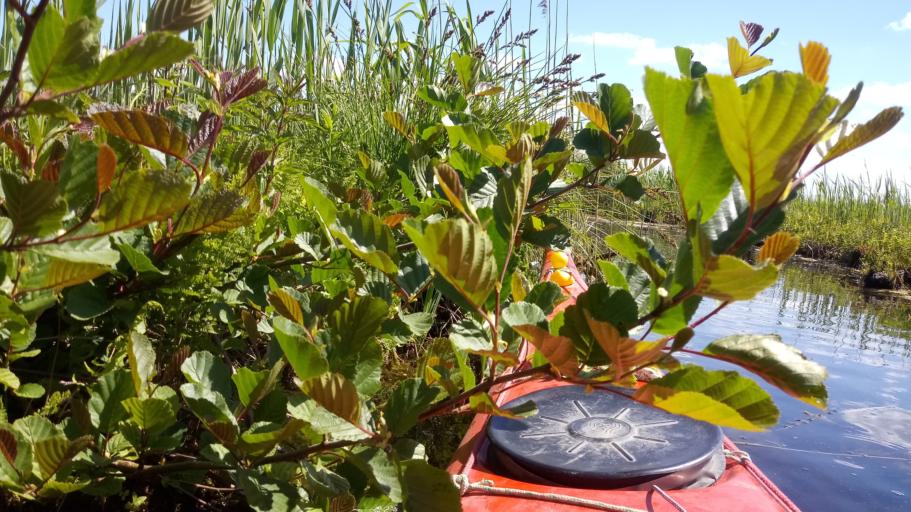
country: NL
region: South Holland
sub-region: Gemeente Nieuwkoop
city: Nieuwkoop
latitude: 52.1423
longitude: 4.7855
